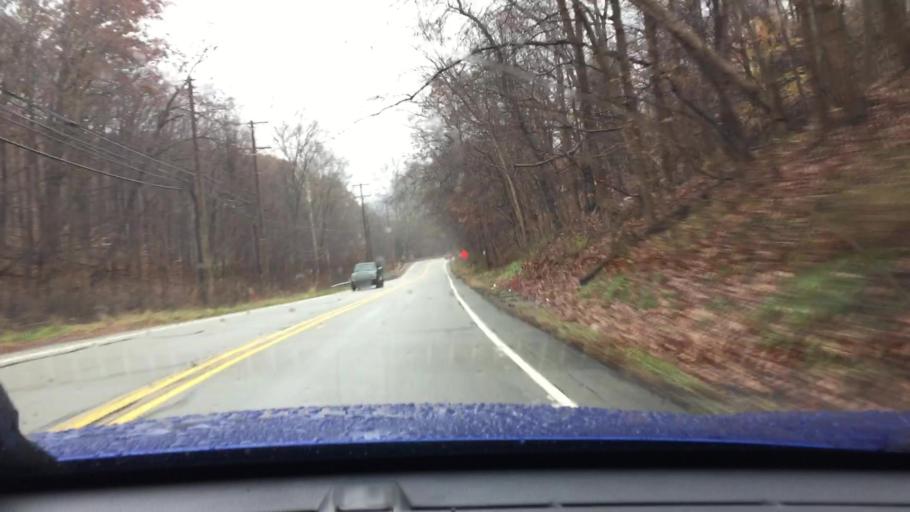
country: US
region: Pennsylvania
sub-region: Washington County
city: Canonsburg
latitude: 40.2879
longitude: -80.1556
